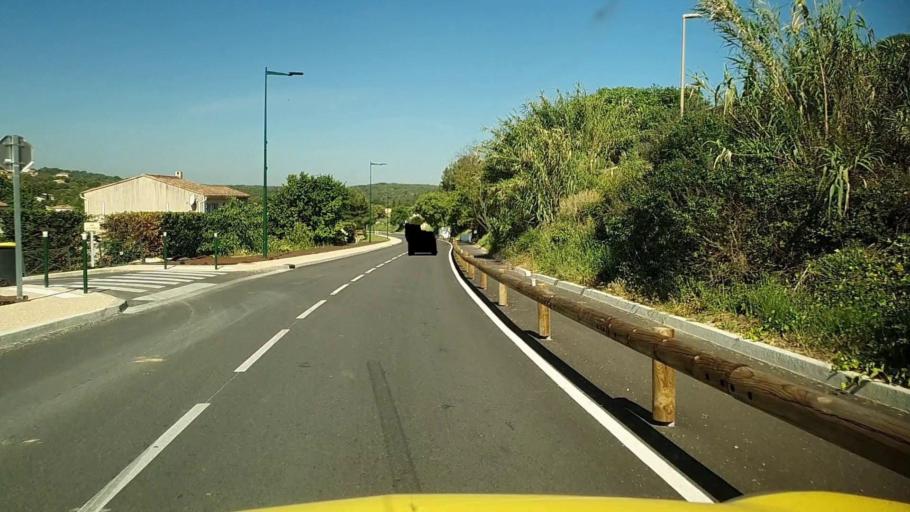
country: FR
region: Languedoc-Roussillon
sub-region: Departement du Gard
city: Poulx
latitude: 43.9106
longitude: 4.4153
